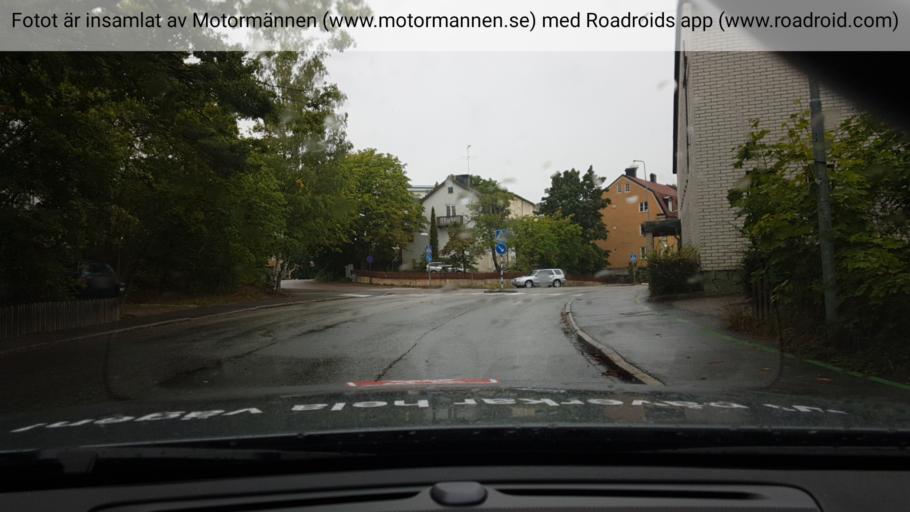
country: SE
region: Stockholm
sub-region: Nynashamns Kommun
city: Nynashamn
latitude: 58.9060
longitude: 17.9528
